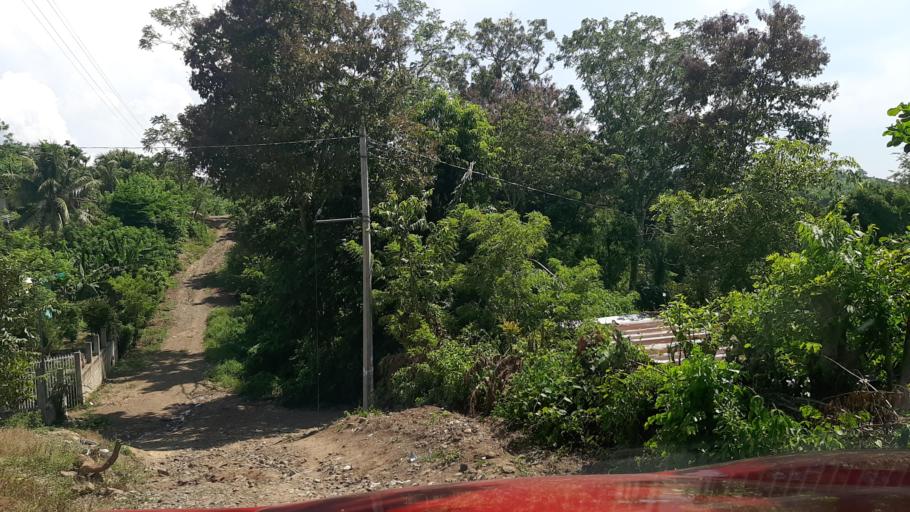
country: MX
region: Veracruz
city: Cazones de Herrera
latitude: 20.6782
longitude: -97.3239
